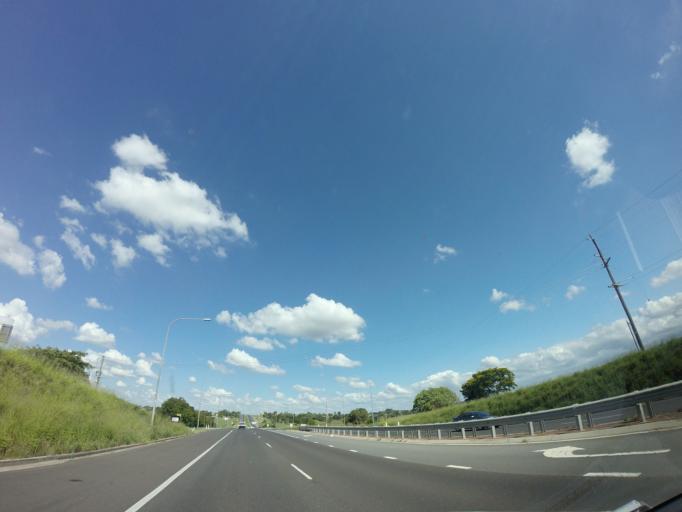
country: AU
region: Queensland
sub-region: Ipswich
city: Thagoona
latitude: -27.5667
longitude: 152.6127
